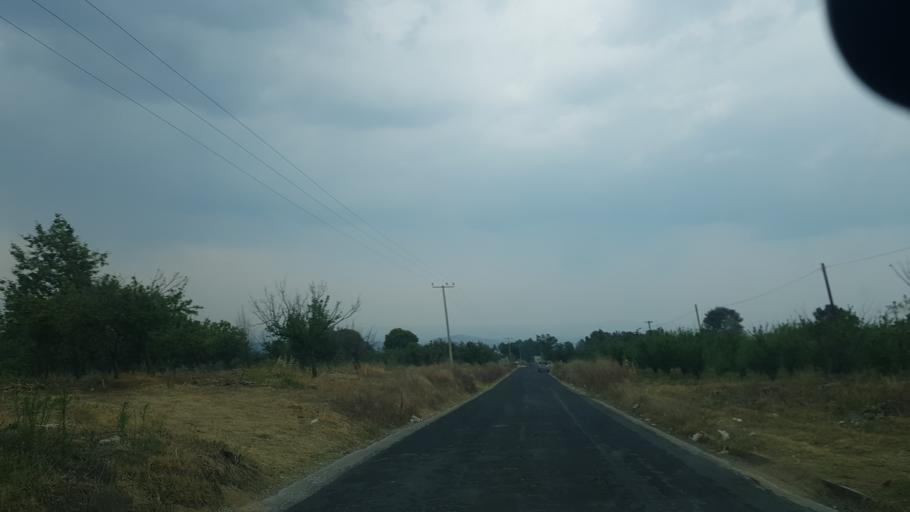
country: MX
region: Puebla
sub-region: Chiautzingo
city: San Nicolas Zecalacoayan
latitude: 19.1846
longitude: -98.4796
